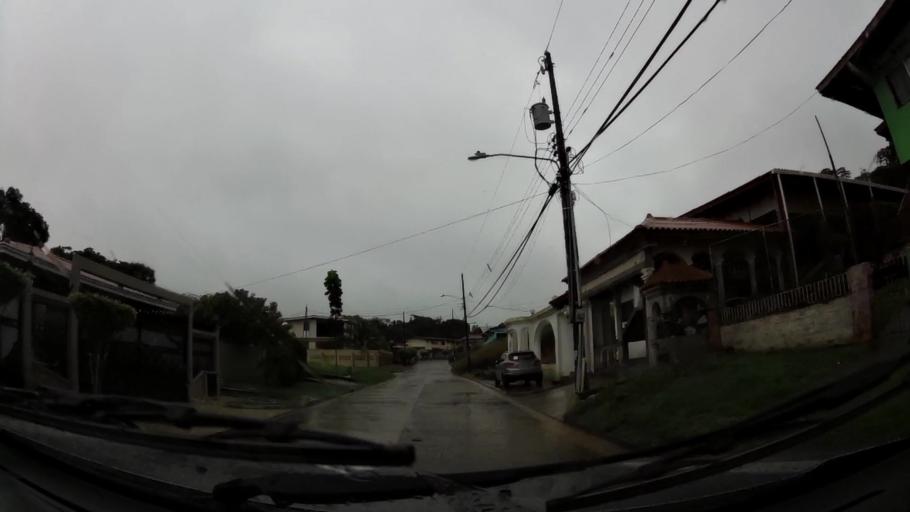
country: PA
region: Colon
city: Sabanitas
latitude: 9.3400
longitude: -79.8076
